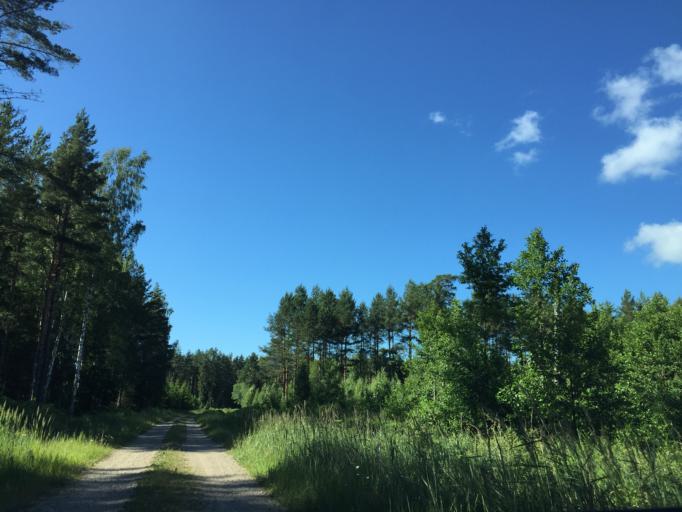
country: LV
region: Ventspils
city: Ventspils
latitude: 57.5450
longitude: 21.7679
